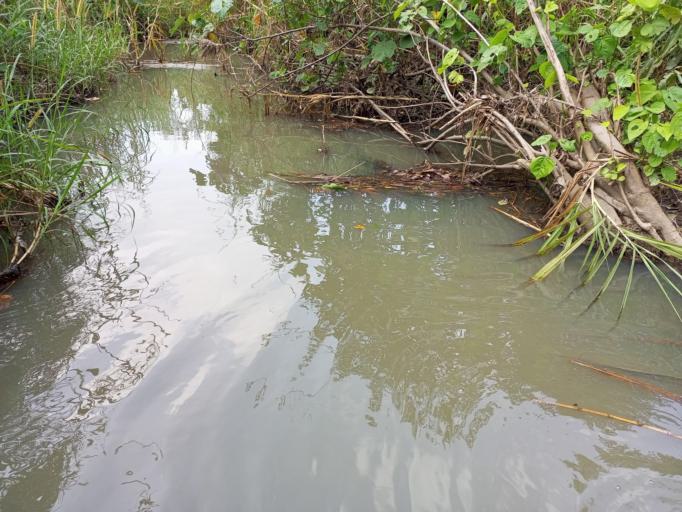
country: CD
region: Eastern Province
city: Bunia
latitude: 1.5379
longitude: 30.2949
